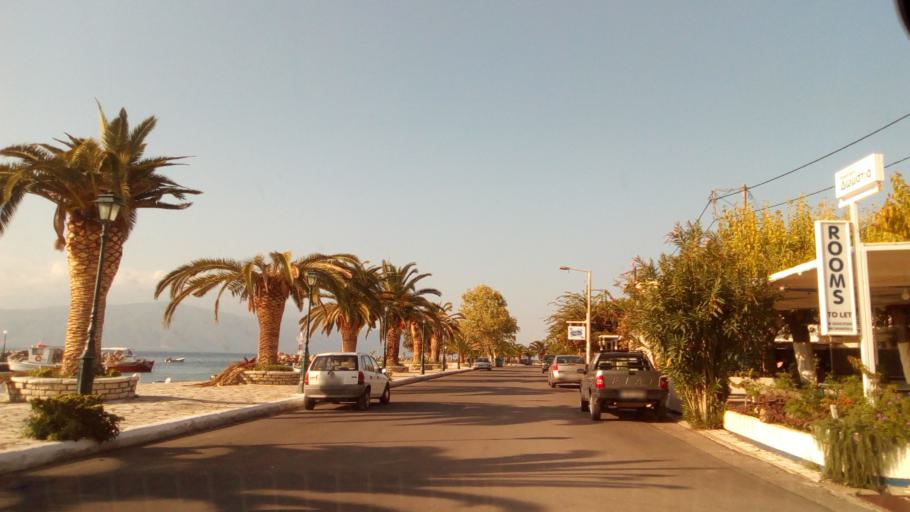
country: GR
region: West Greece
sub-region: Nomos Achaias
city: Kamarai
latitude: 38.3916
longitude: 22.0139
